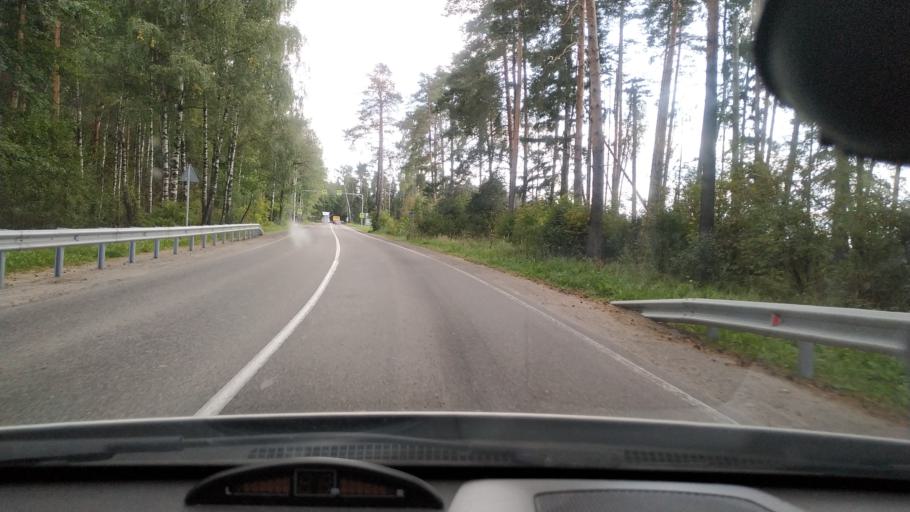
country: RU
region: Moskovskaya
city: Zheleznodorozhnyy
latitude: 55.7893
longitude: 38.0367
